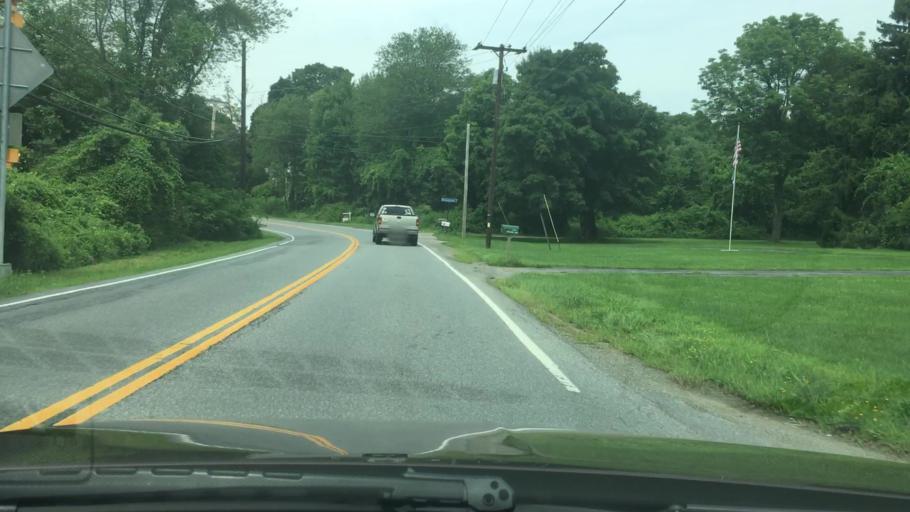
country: US
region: New York
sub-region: Dutchess County
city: Red Oaks Mill
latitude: 41.6532
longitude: -73.8381
